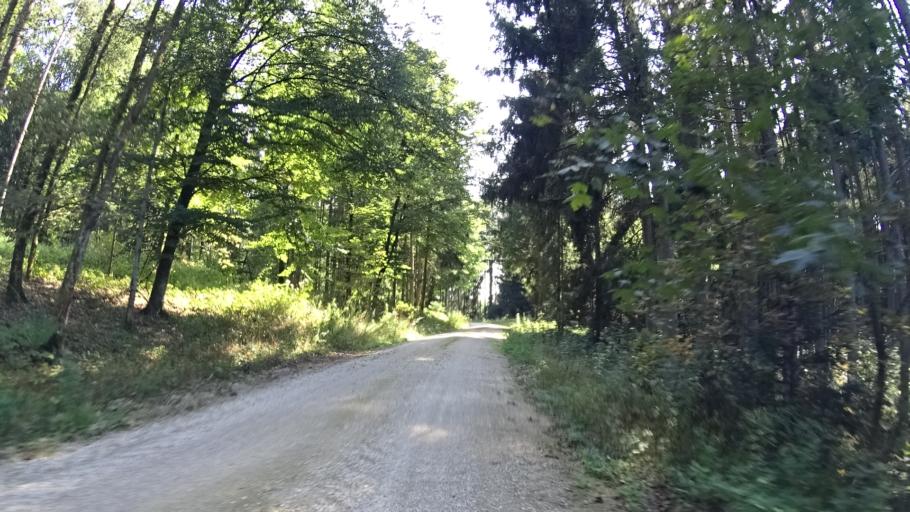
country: DE
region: Bavaria
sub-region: Upper Bavaria
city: Walting
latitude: 48.9419
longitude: 11.2569
